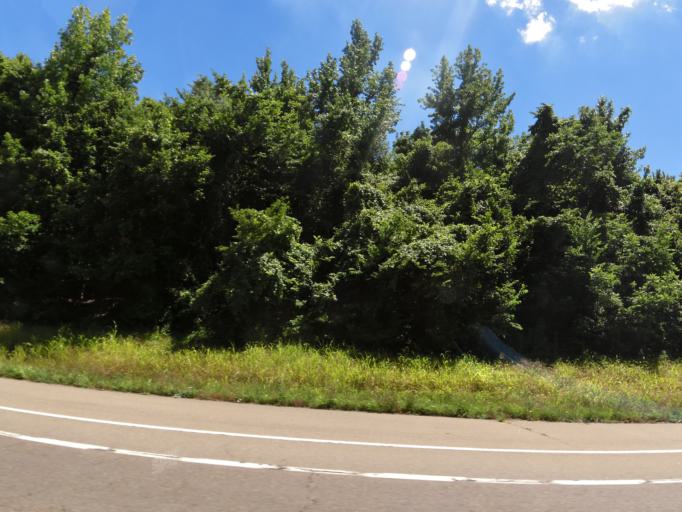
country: US
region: Tennessee
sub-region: Dyer County
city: Dyersburg
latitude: 36.0736
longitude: -89.4822
